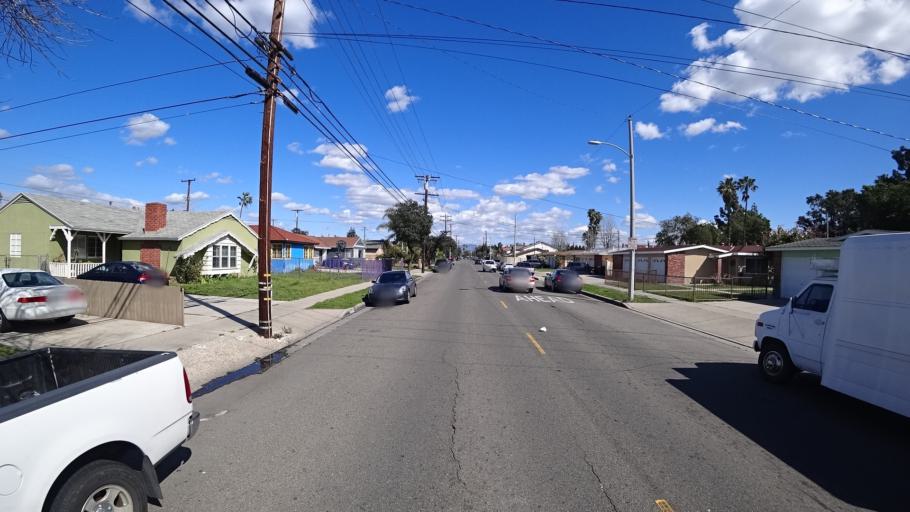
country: US
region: California
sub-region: Orange County
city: Anaheim
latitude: 33.8509
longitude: -117.8948
